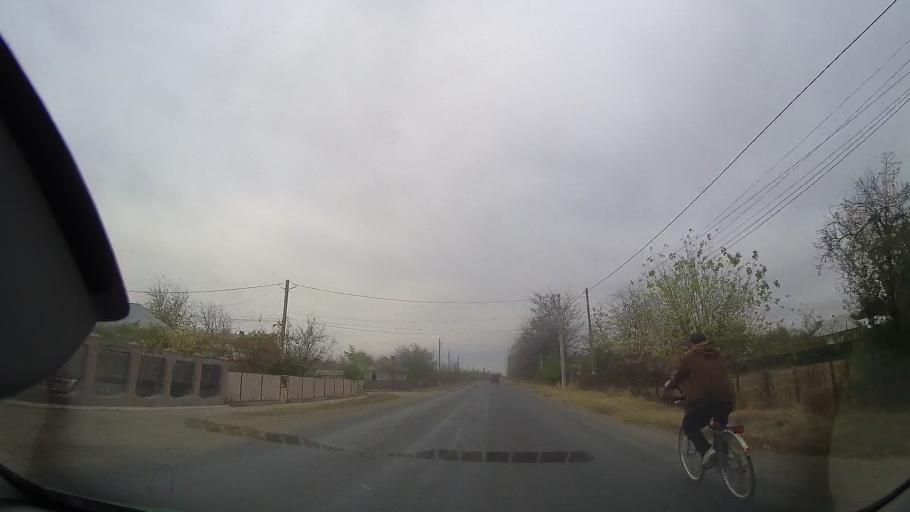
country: RO
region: Buzau
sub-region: Comuna Padina
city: Padina
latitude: 44.8342
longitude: 27.1088
